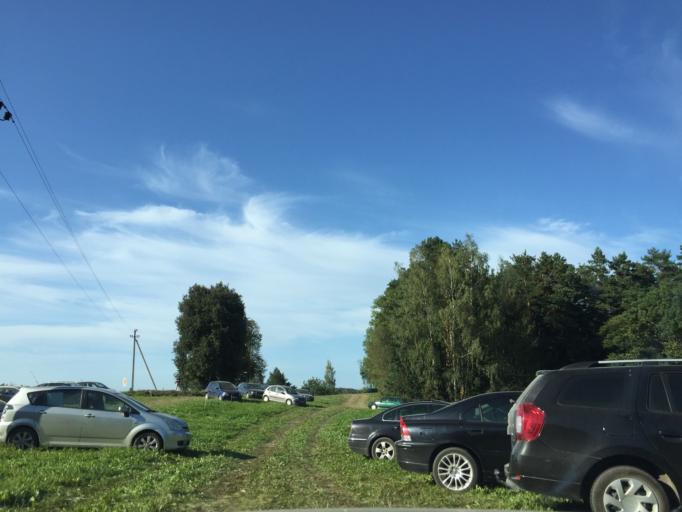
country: LT
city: Zarasai
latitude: 55.7871
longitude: 25.9541
